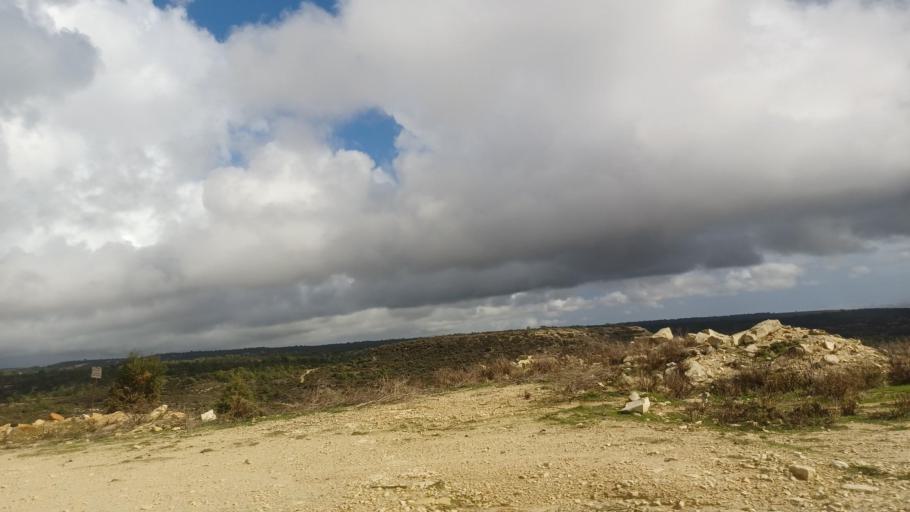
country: CY
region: Limassol
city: Sotira
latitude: 34.7277
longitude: 32.8317
